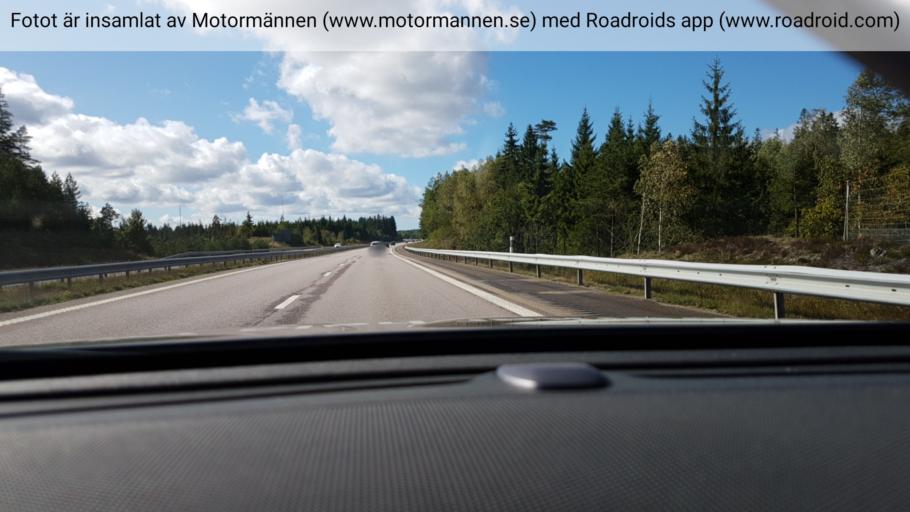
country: SE
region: Vaestra Goetaland
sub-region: Boras Kommun
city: Sandared
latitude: 57.6843
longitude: 12.7672
